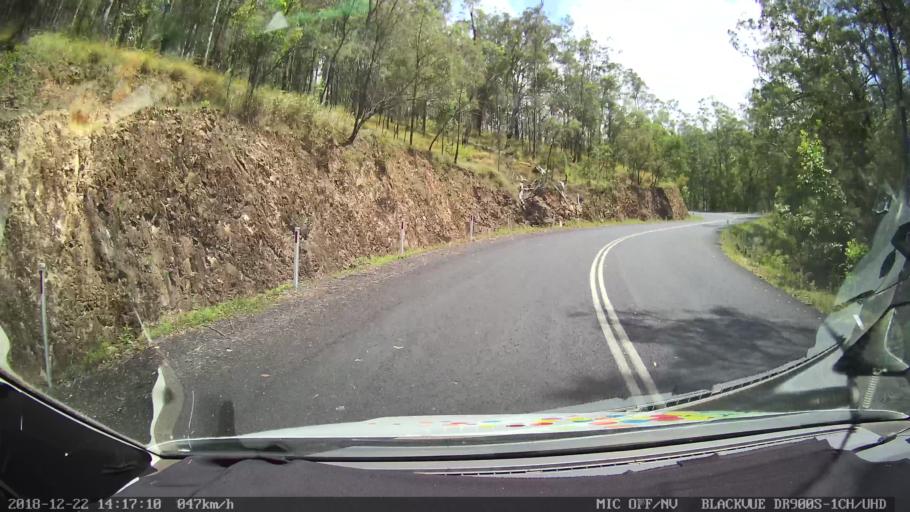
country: AU
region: New South Wales
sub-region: Clarence Valley
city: Coutts Crossing
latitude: -30.0070
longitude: 152.6686
